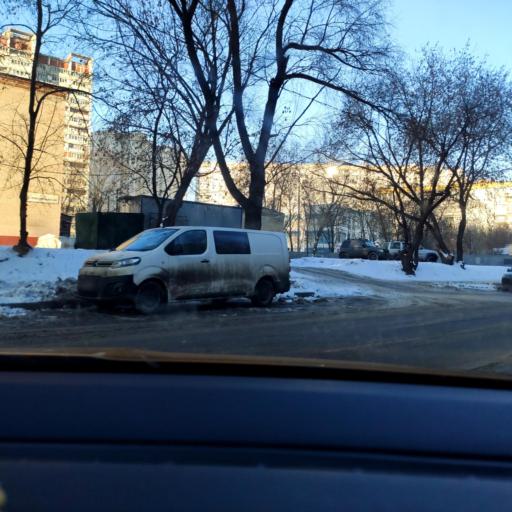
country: RU
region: Moscow
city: Mar'ino
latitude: 55.6748
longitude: 37.7196
